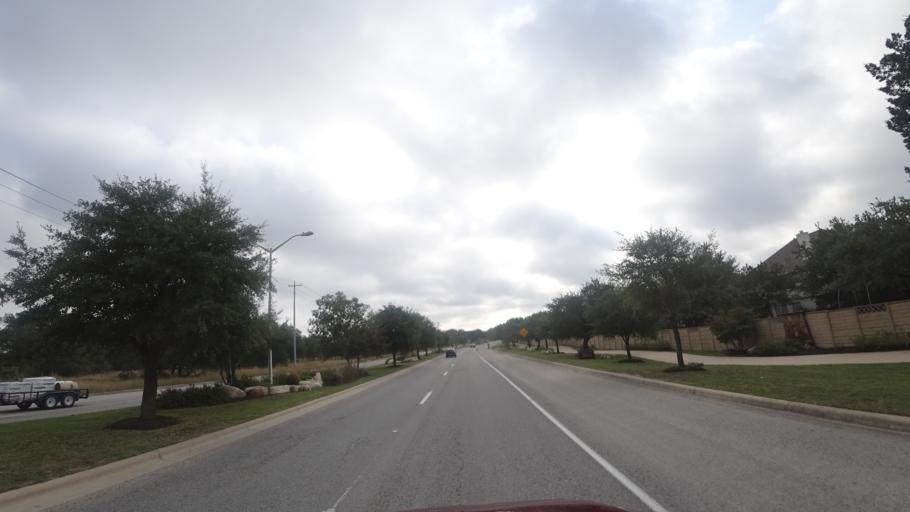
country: US
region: Texas
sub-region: Williamson County
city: Cedar Park
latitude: 30.4868
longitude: -97.8554
